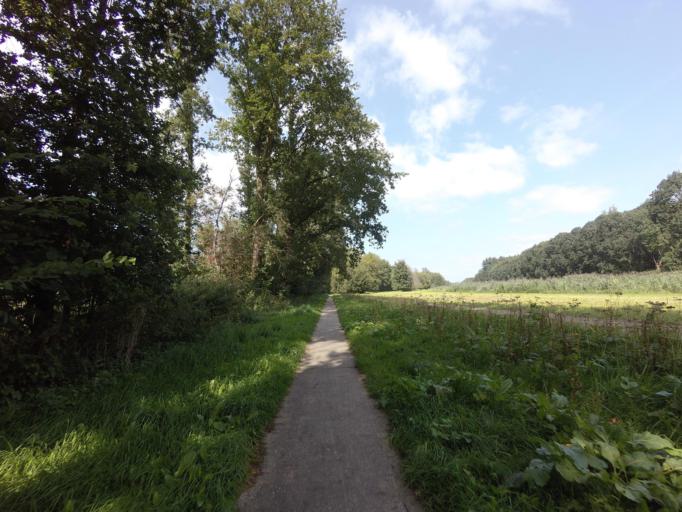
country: NL
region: Flevoland
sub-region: Gemeente Lelystad
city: Lelystad
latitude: 52.5043
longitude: 5.5223
